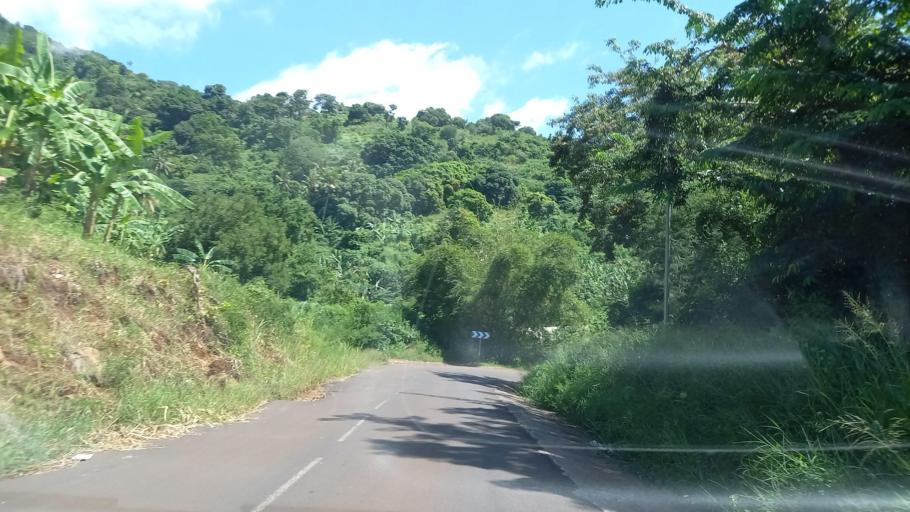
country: YT
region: Bandraboua
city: Bandraboua
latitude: -12.6848
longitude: 45.0999
